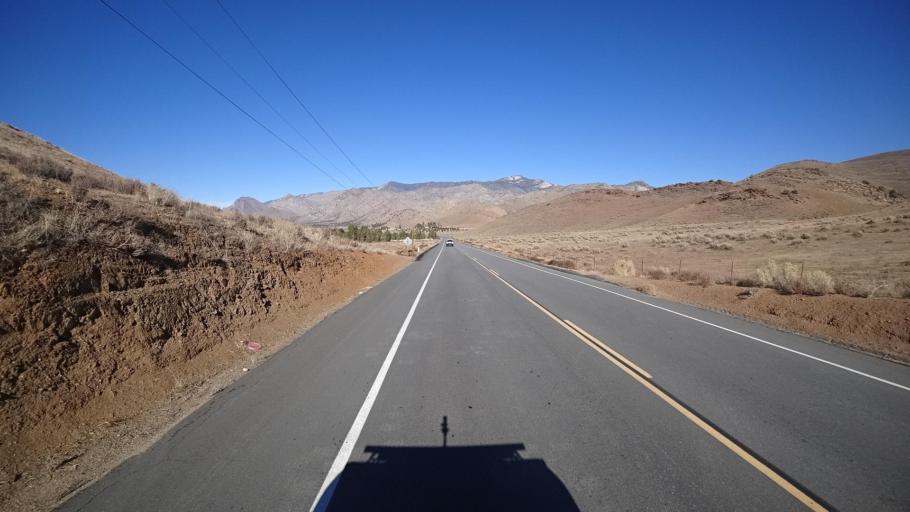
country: US
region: California
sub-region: Kern County
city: Wofford Heights
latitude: 35.6973
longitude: -118.4257
